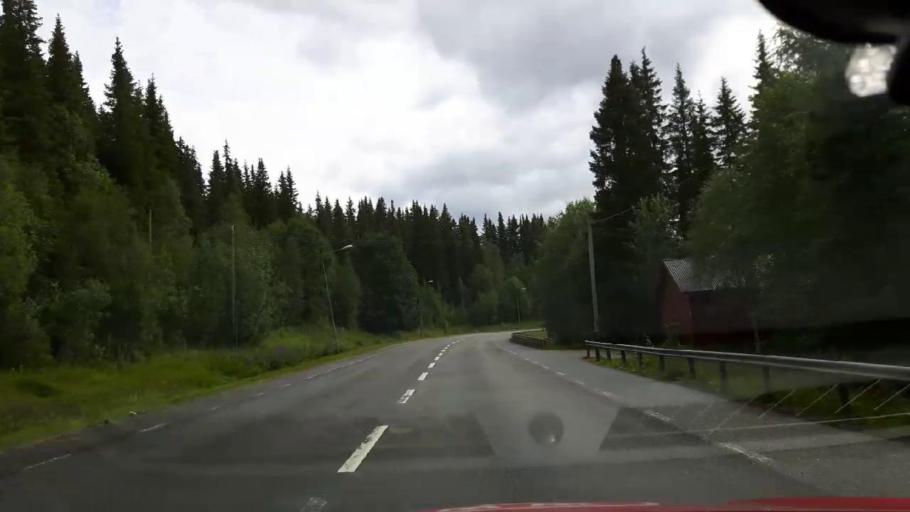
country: NO
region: Nord-Trondelag
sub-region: Lierne
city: Sandvika
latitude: 64.4923
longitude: 14.1503
